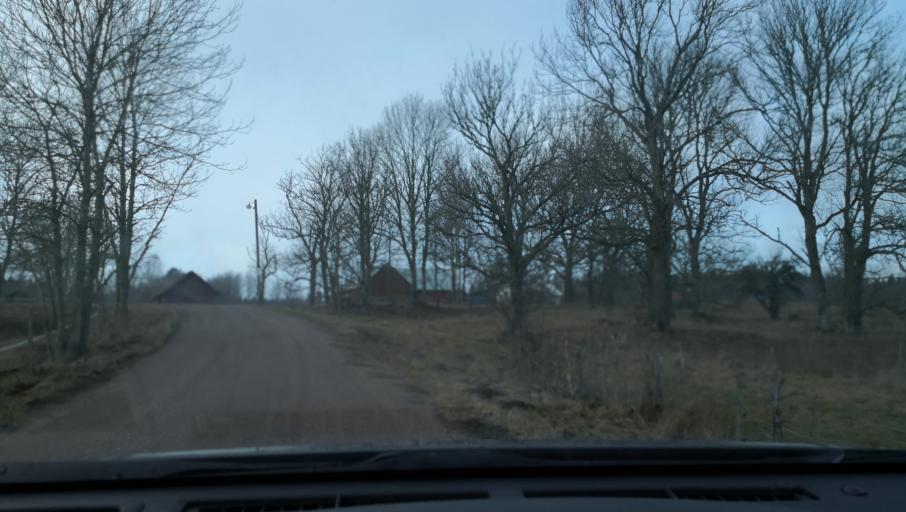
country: SE
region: Vaestra Goetaland
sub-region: Gullspangs Kommun
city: Gullspang
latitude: 58.9594
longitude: 14.0907
